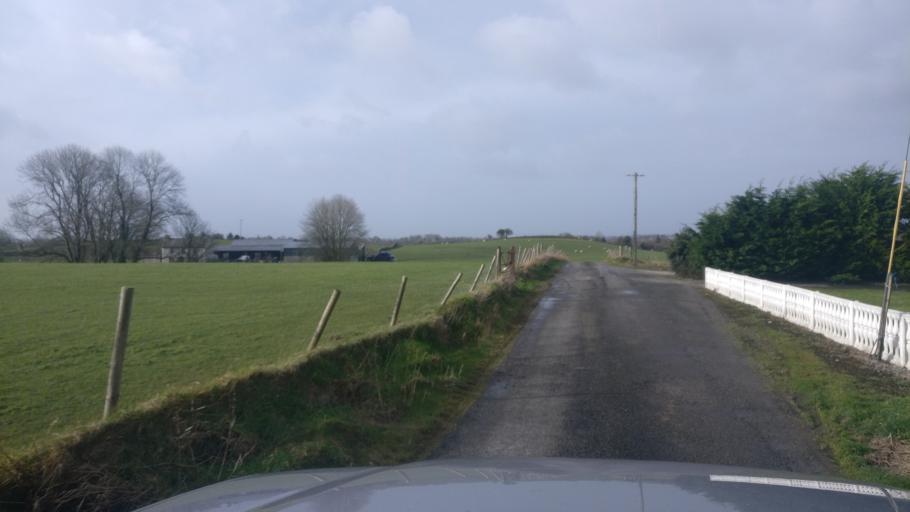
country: IE
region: Connaught
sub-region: County Galway
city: Loughrea
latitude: 53.2786
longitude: -8.5879
